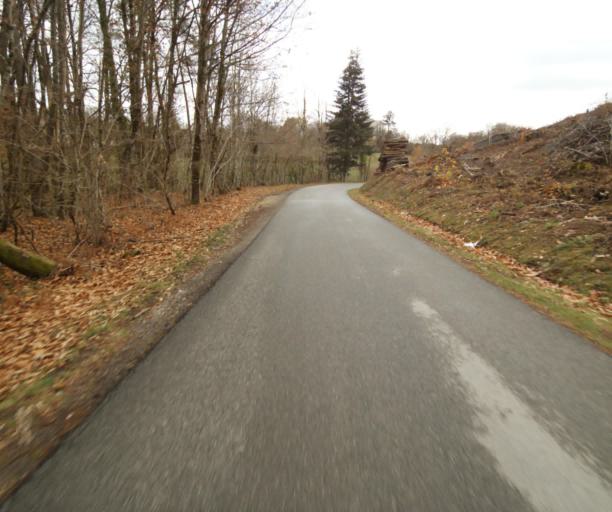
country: FR
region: Limousin
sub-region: Departement de la Correze
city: Saint-Mexant
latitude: 45.2860
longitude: 1.6496
